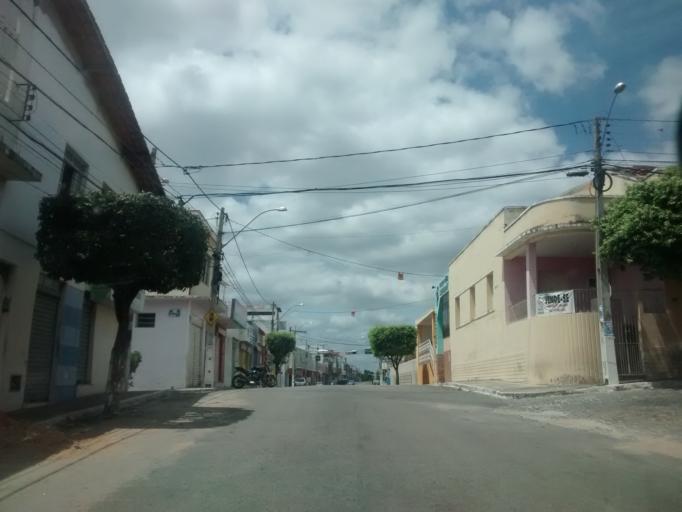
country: BR
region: Bahia
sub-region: Brumado
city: Brumado
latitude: -14.2044
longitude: -41.6649
